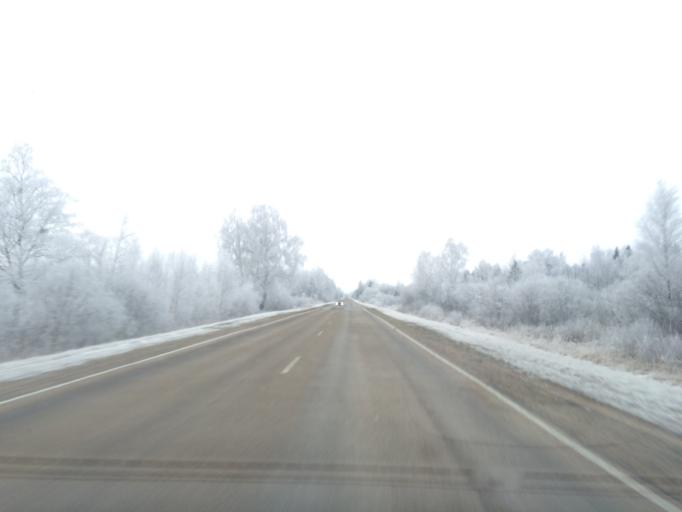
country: LV
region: Karsava
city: Karsava
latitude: 56.6505
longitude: 27.4963
